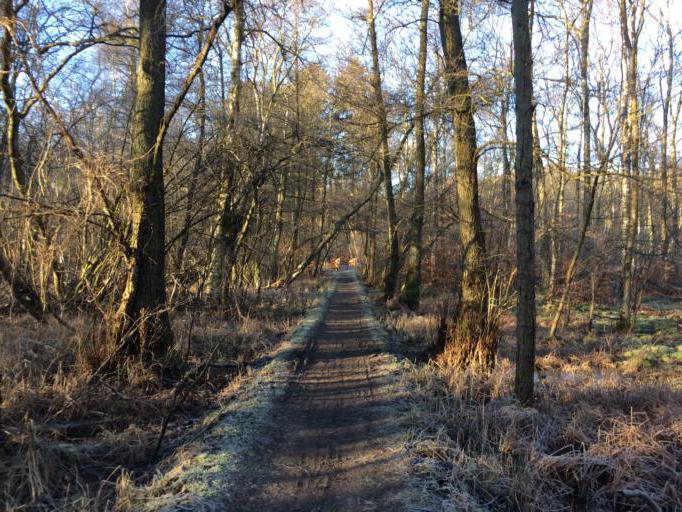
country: DK
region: Capital Region
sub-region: Gladsaxe Municipality
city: Buddinge
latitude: 55.7790
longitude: 12.4621
